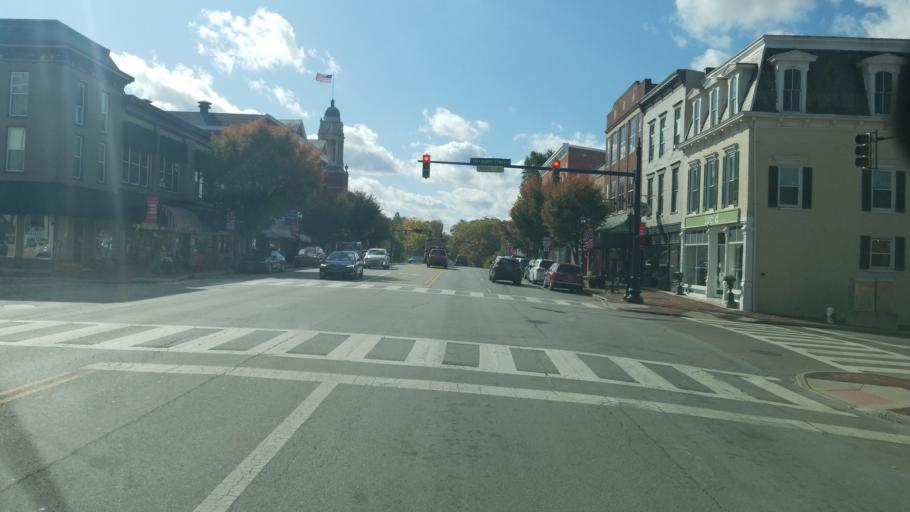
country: US
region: Ohio
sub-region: Warren County
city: Lebanon
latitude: 39.4348
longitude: -84.2083
